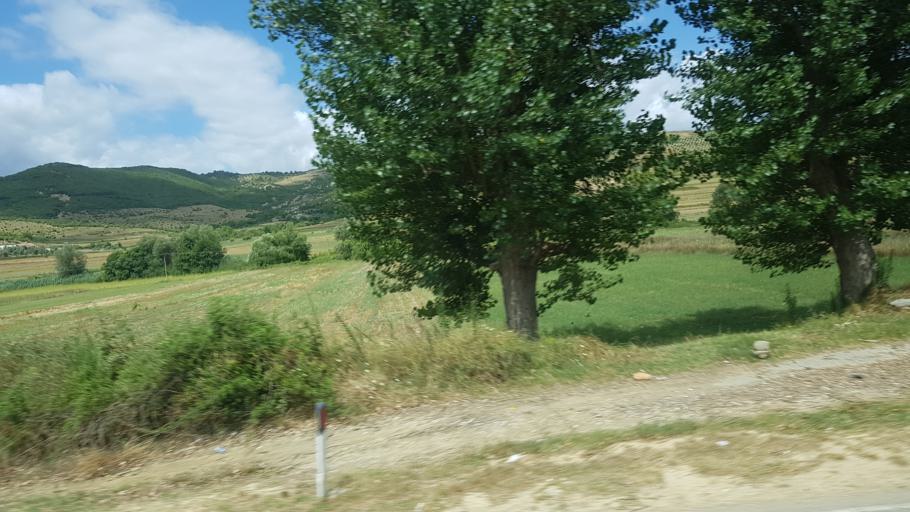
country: AL
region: Gjirokaster
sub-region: Rrethi i Tepelenes
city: Krahes
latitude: 40.4189
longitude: 19.8576
